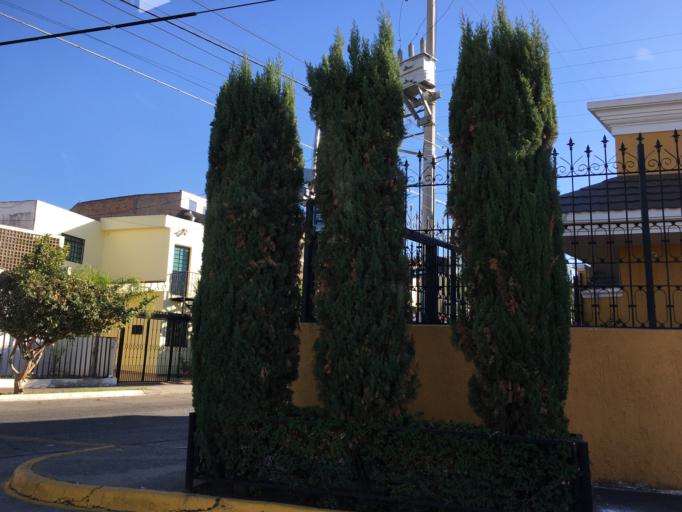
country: MX
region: Jalisco
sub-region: Zapopan
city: Zapopan
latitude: 20.7092
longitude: -103.3417
